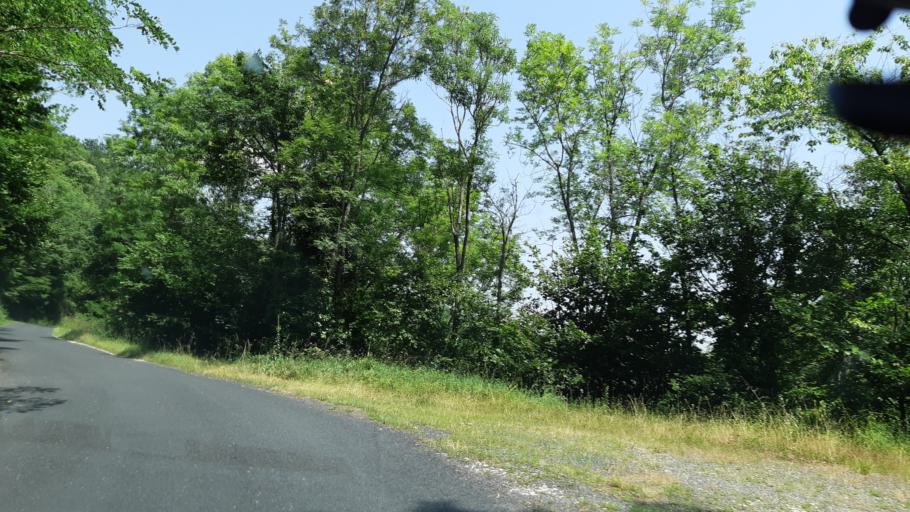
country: FR
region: Languedoc-Roussillon
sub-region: Departement des Pyrenees-Orientales
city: Arles
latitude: 42.5320
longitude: 2.5891
